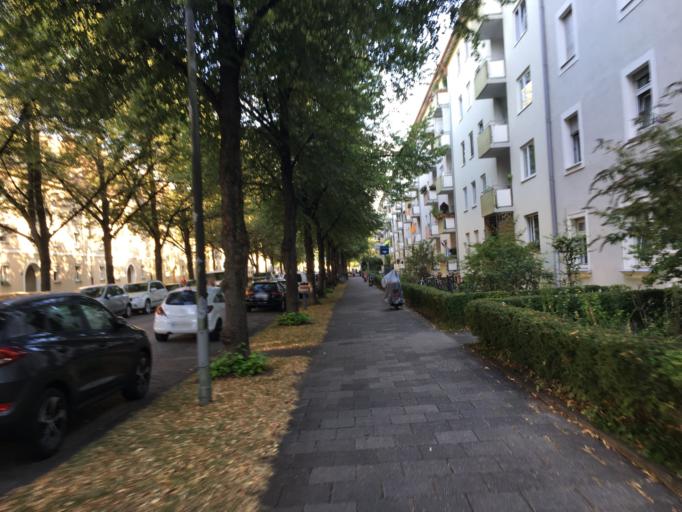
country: DE
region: Bavaria
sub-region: Upper Bavaria
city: Munich
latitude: 48.1649
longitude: 11.5627
